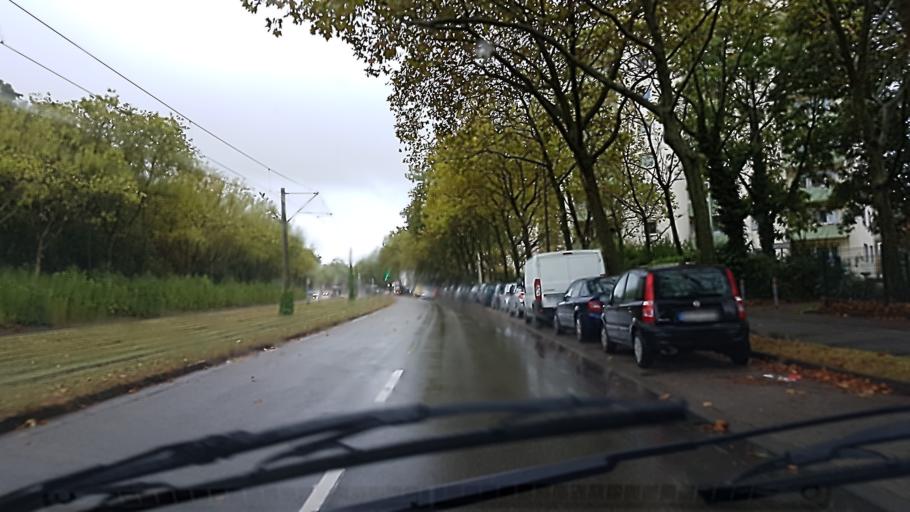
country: DE
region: Baden-Wuerttemberg
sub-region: Freiburg Region
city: Freiburg
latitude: 48.0078
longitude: 7.8161
